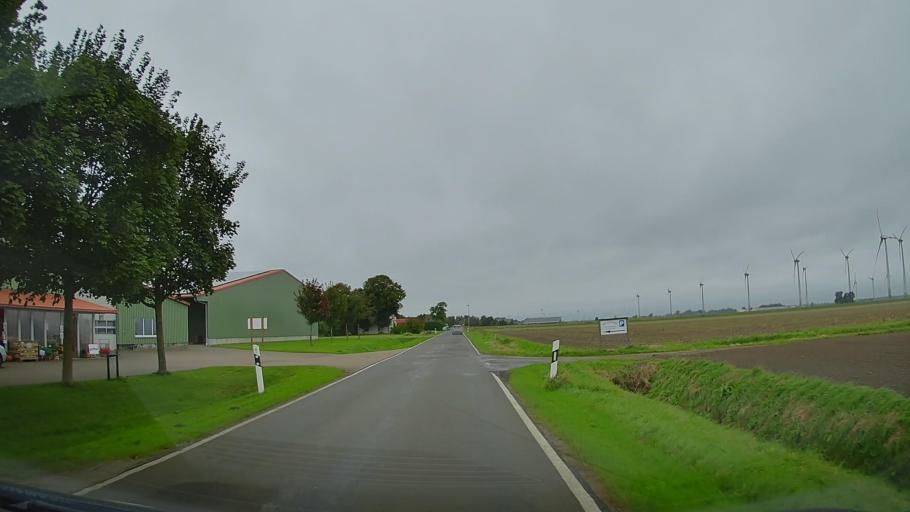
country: DE
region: Schleswig-Holstein
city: Neufeld
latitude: 53.9126
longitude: 9.0031
